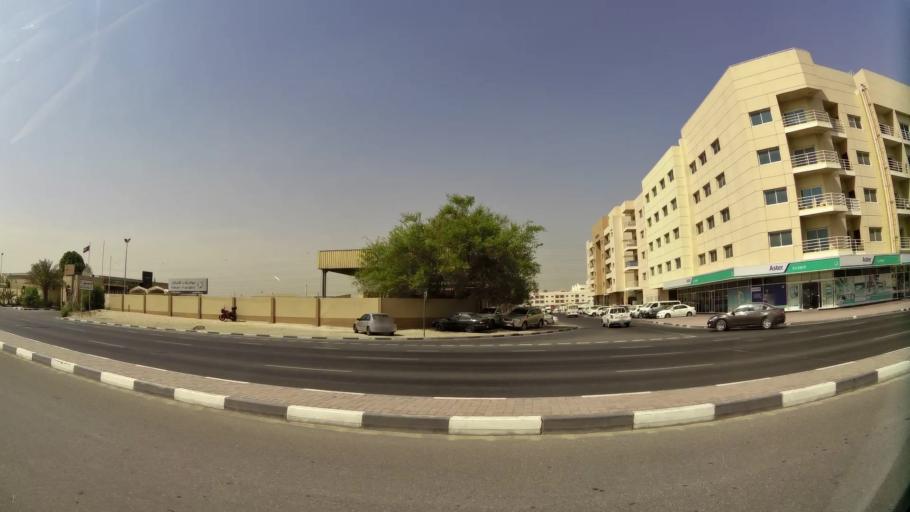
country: AE
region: Ash Shariqah
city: Sharjah
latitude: 25.2769
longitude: 55.3859
